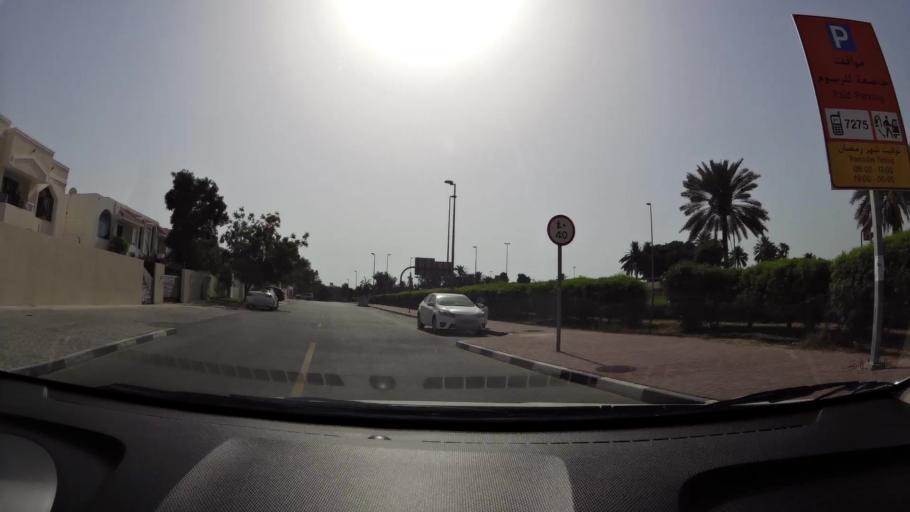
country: AE
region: Ash Shariqah
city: Sharjah
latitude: 25.2444
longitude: 55.3557
